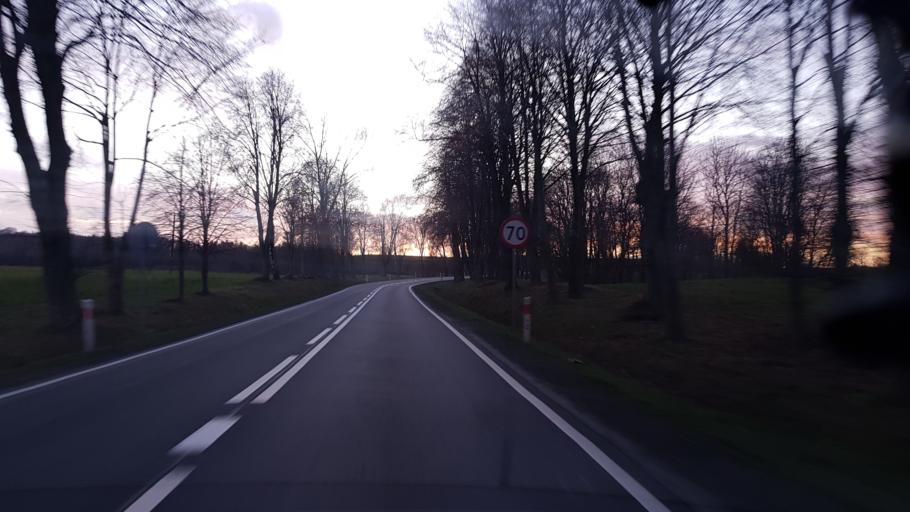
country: PL
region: Pomeranian Voivodeship
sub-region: Powiat bytowski
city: Tuchomie
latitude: 54.1334
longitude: 17.4054
